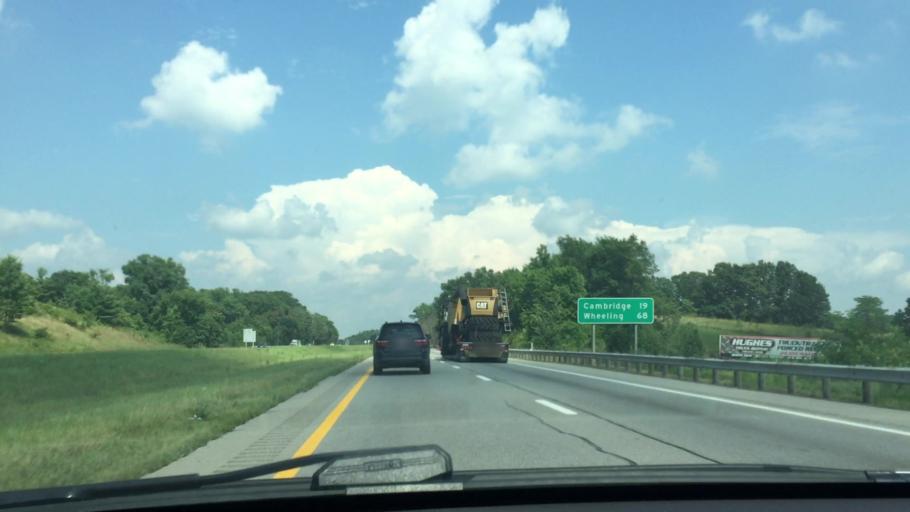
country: US
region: Ohio
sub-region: Muskingum County
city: Pleasant Grove
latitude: 39.9696
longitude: -81.8793
